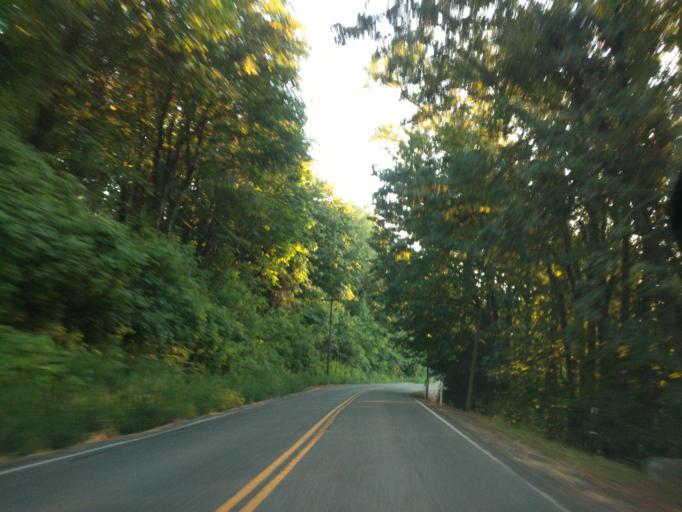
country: US
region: Washington
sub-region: Whatcom County
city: Sumas
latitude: 48.9709
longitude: -122.2305
